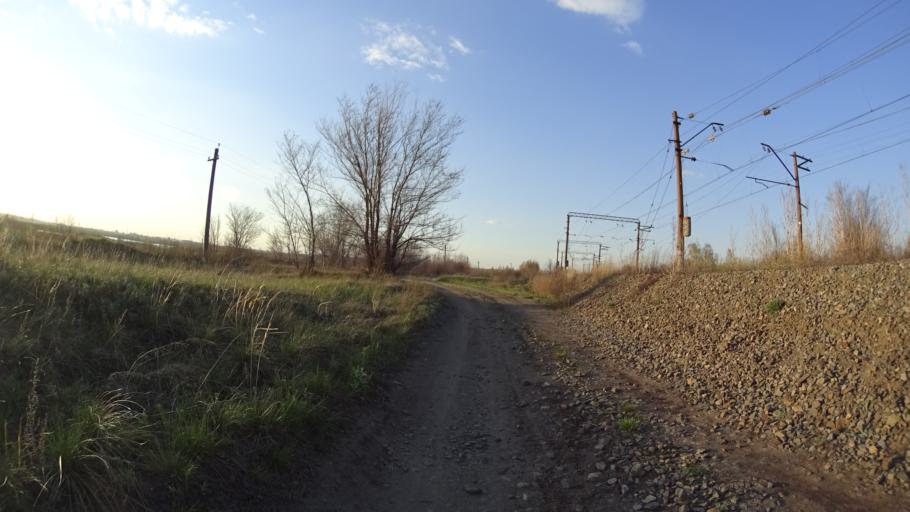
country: RU
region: Chelyabinsk
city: Troitsk
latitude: 54.0613
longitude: 61.6137
